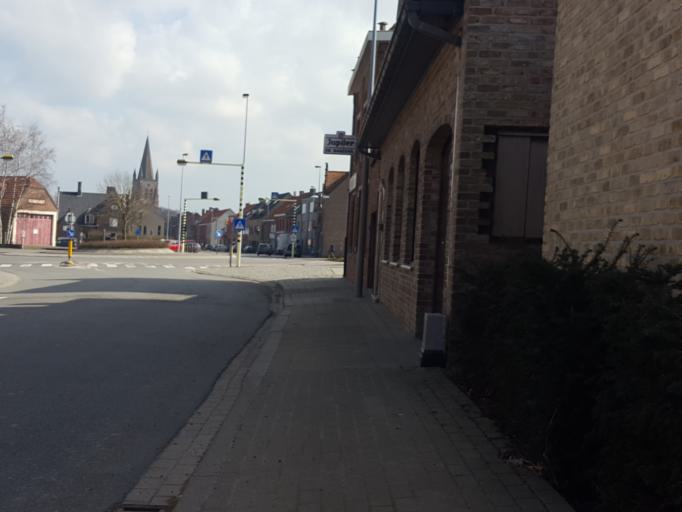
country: BE
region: Flanders
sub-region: Provincie West-Vlaanderen
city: Ieper
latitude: 50.9143
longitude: 2.9120
